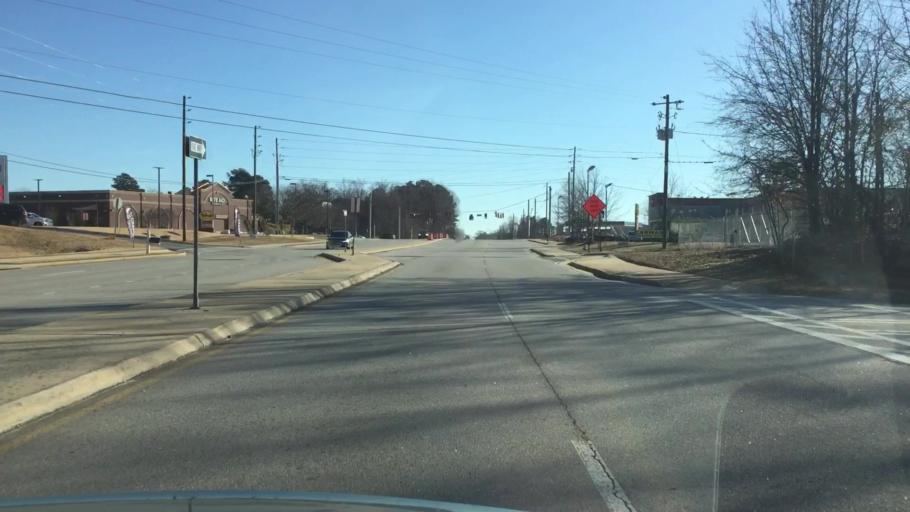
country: US
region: Georgia
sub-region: Henry County
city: McDonough
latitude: 33.5076
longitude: -84.1430
